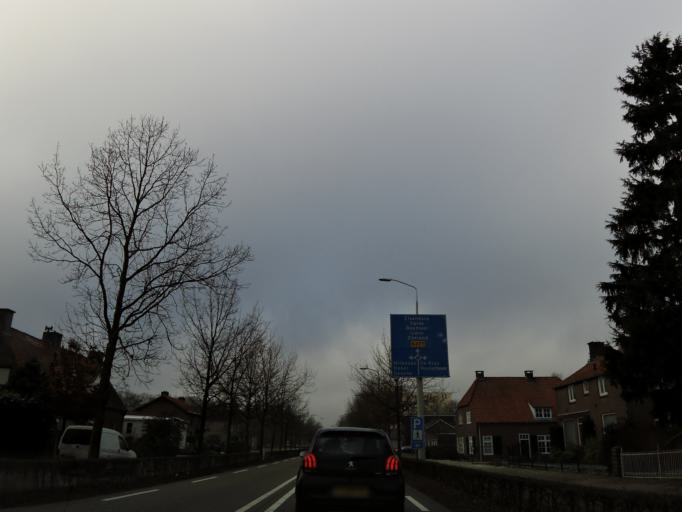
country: NL
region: North Brabant
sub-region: Gemeente Sint Anthonis
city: Sint Anthonis
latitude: 51.5484
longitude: 5.8100
